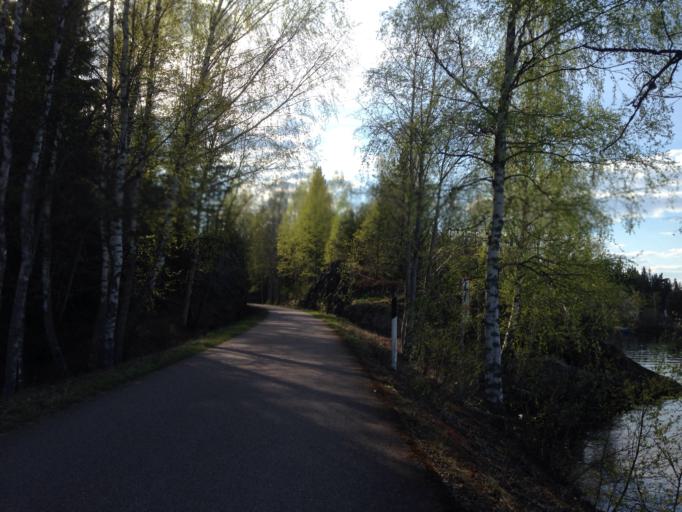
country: SE
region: Dalarna
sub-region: Ludvika Kommun
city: Ludvika
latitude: 60.1452
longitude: 15.1552
